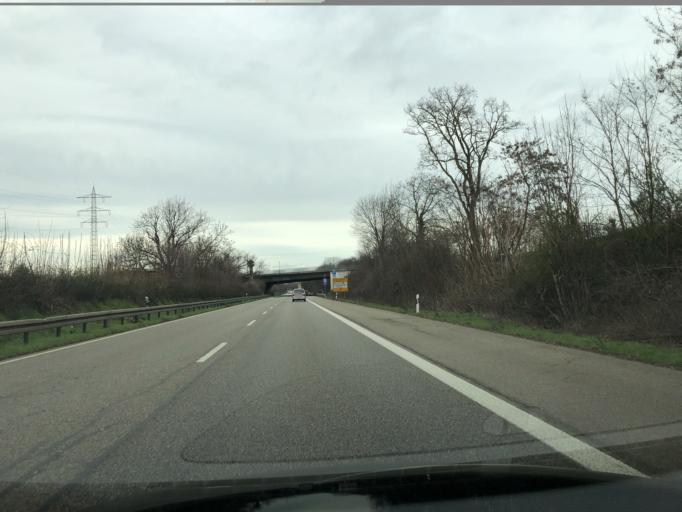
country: DE
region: Baden-Wuerttemberg
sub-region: Freiburg Region
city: Freiburg
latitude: 48.0002
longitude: 7.8168
